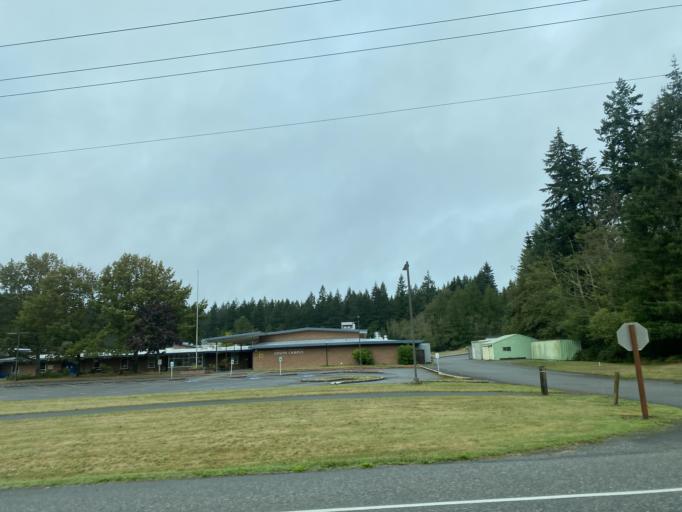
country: US
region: Washington
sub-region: Island County
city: Langley
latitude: 48.0129
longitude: -122.4096
